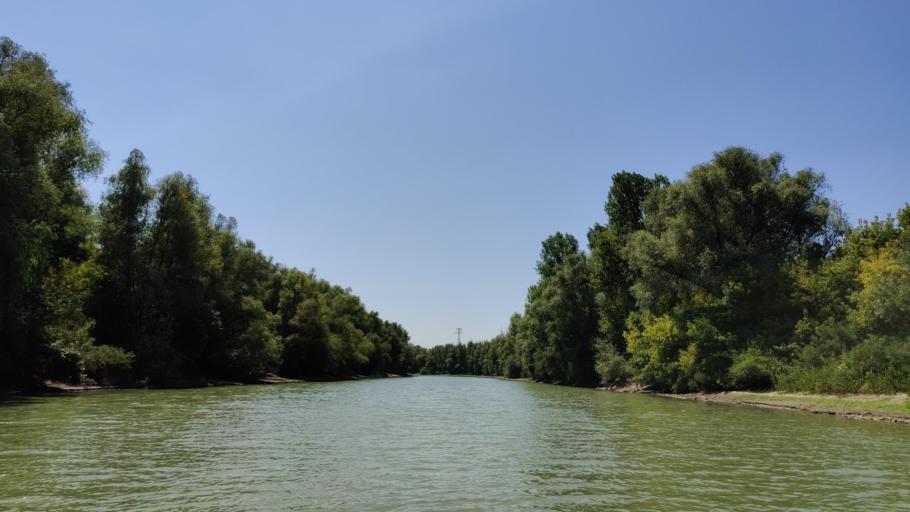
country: RO
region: Tulcea
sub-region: Municipiul Tulcea
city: Tulcea
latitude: 45.2090
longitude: 28.8569
